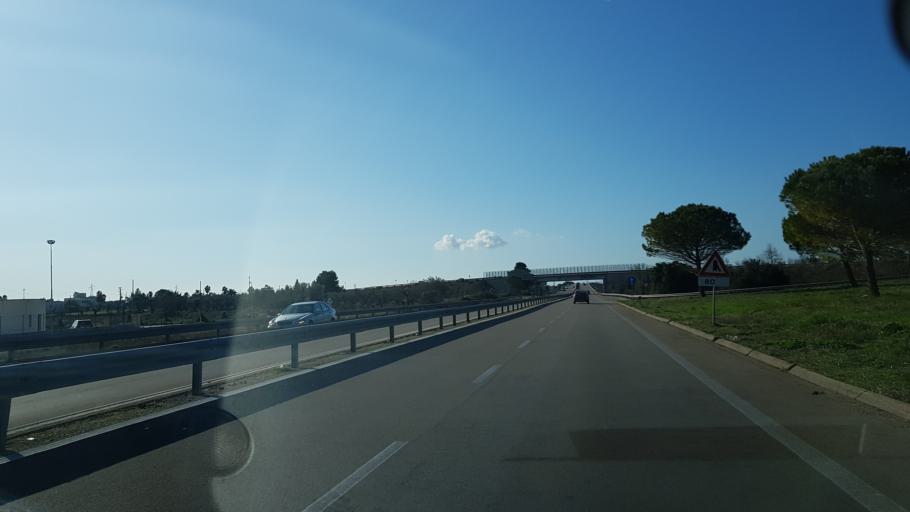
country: IT
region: Apulia
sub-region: Provincia di Lecce
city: Galatone
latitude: 40.1208
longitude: 18.0483
